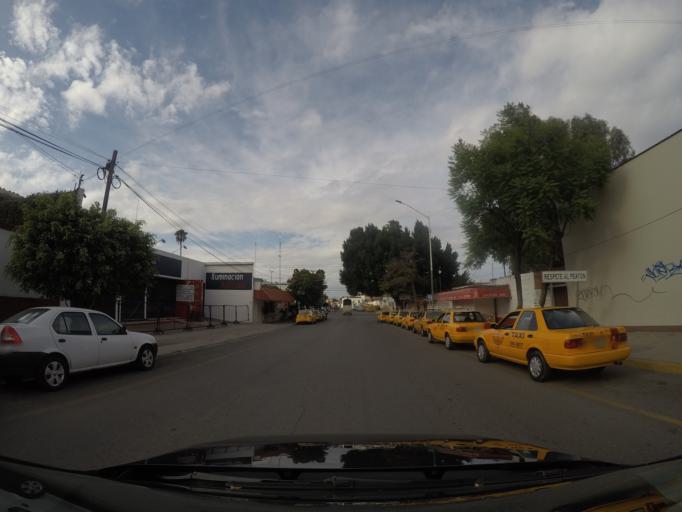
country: MX
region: Oaxaca
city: Oaxaca de Juarez
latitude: 17.0714
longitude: -96.7166
